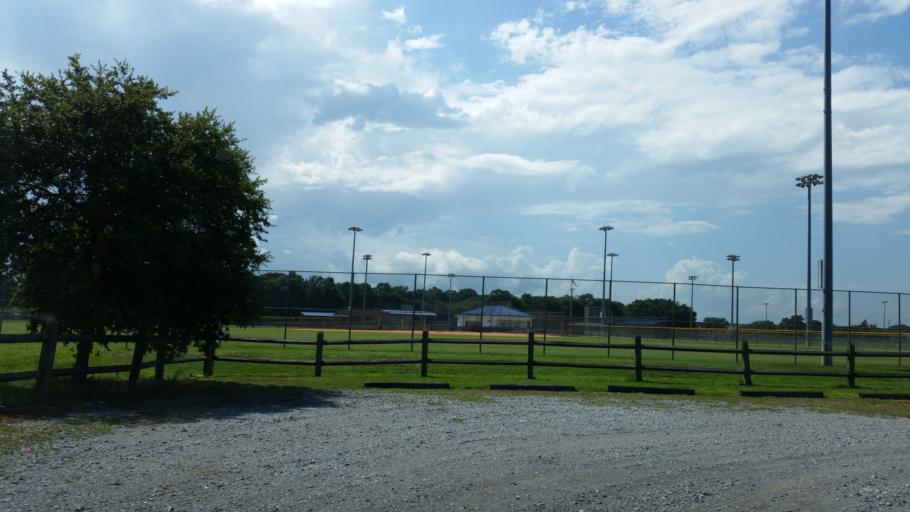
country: US
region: Florida
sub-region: Escambia County
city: Ensley
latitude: 30.5290
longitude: -87.2554
